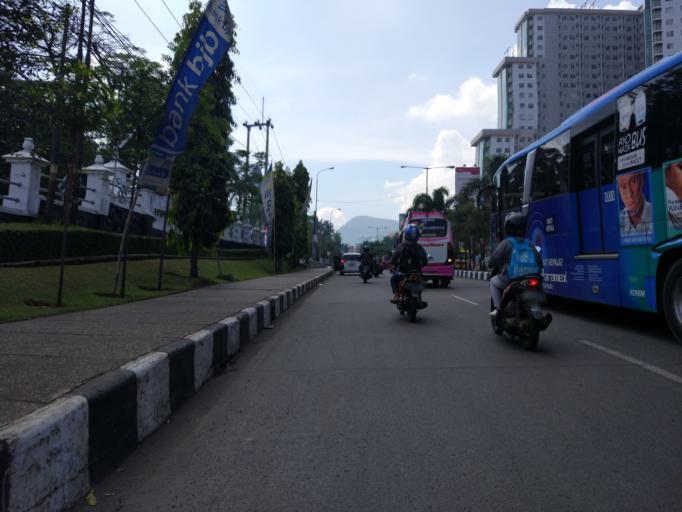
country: ID
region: West Java
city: Cileunyi
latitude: -6.9361
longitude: 107.7636
